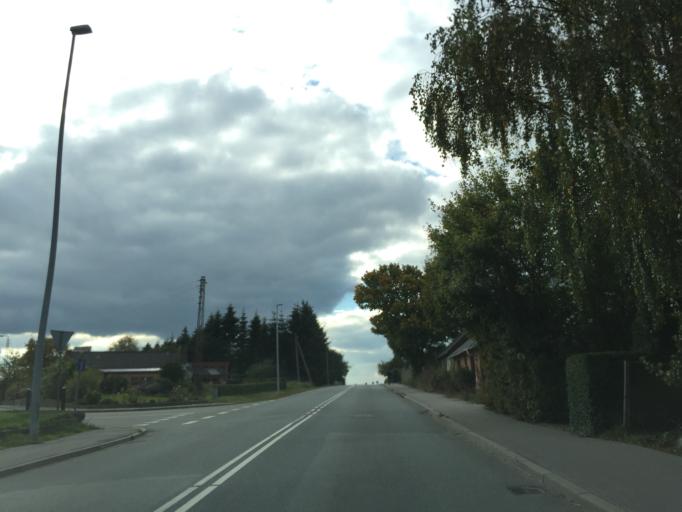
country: DK
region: Central Jutland
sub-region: Randers Kommune
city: Langa
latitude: 56.3435
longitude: 9.8725
